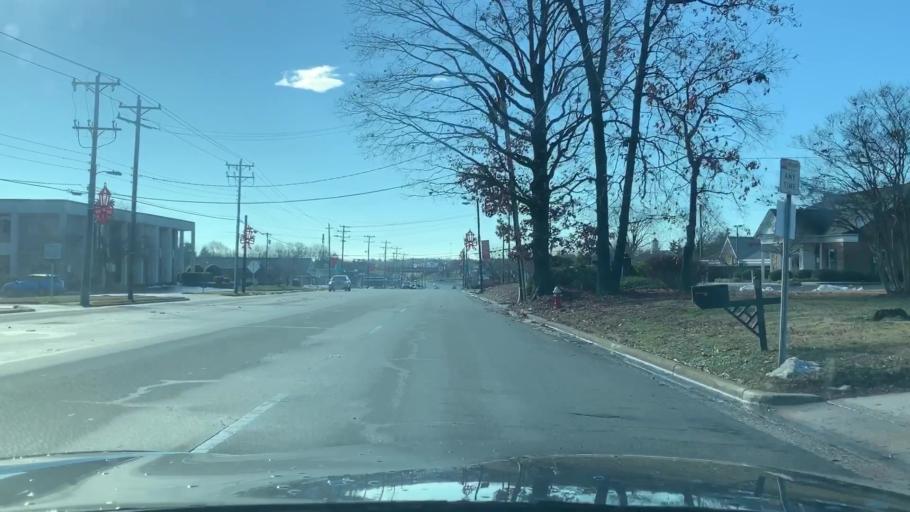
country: US
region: North Carolina
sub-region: Alamance County
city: Graham
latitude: 36.0665
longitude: -79.4005
